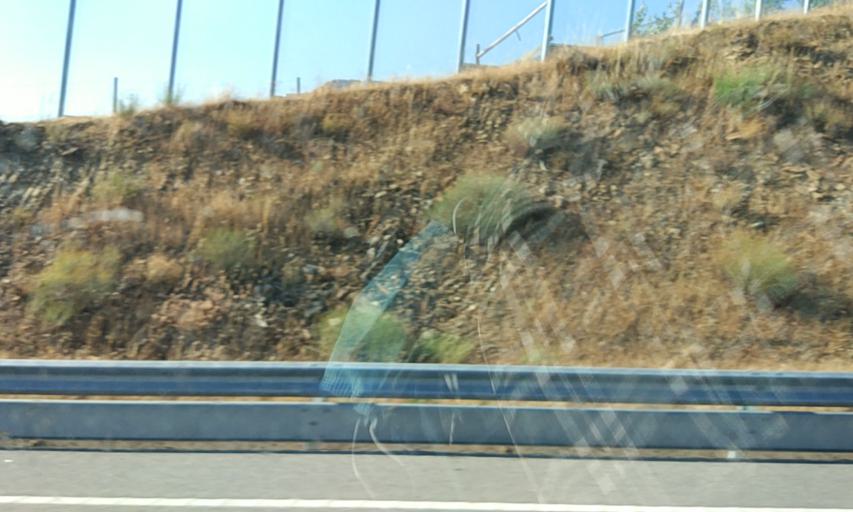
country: PT
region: Vila Real
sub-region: Murca
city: Murca
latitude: 41.4304
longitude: -7.3489
